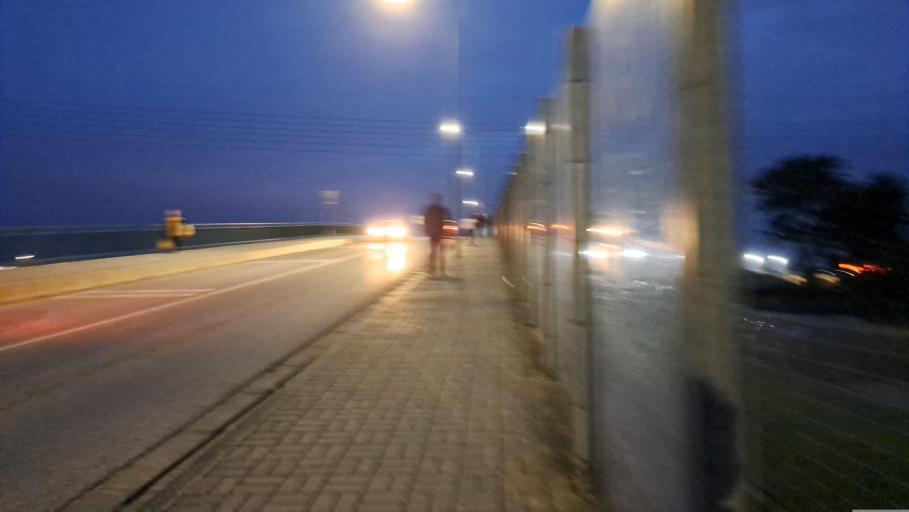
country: PT
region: Setubal
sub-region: Moita
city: Alhos Vedros
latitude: 38.6556
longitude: -9.0378
